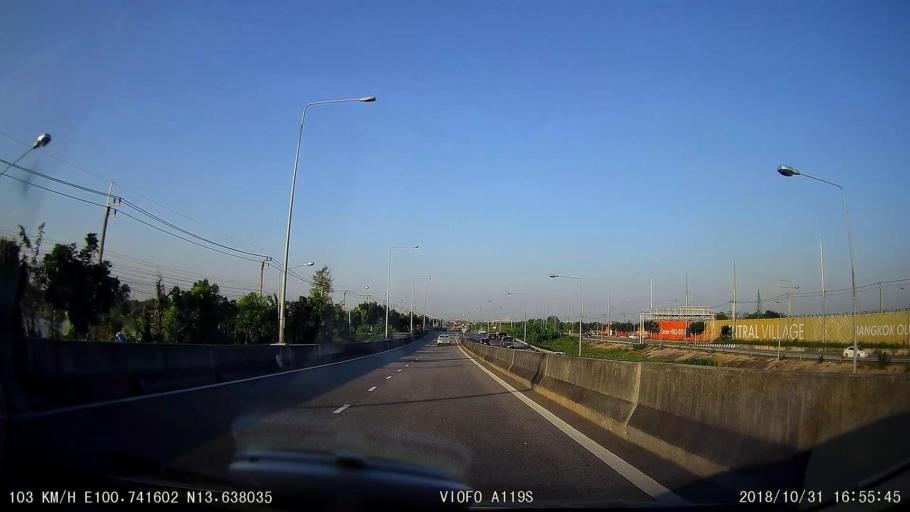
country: TH
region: Samut Prakan
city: Ban Khlong Bang Sao Thong
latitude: 13.6381
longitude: 100.7416
